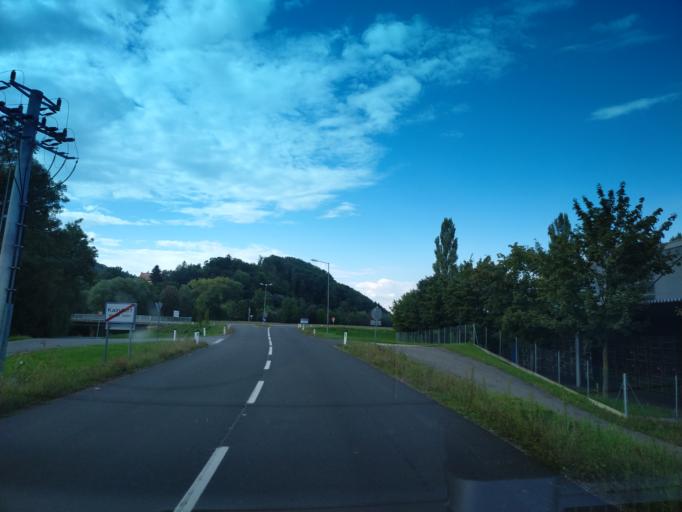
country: AT
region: Styria
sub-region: Politischer Bezirk Leibnitz
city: Kaindorf an der Sulm
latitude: 46.7940
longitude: 15.5317
